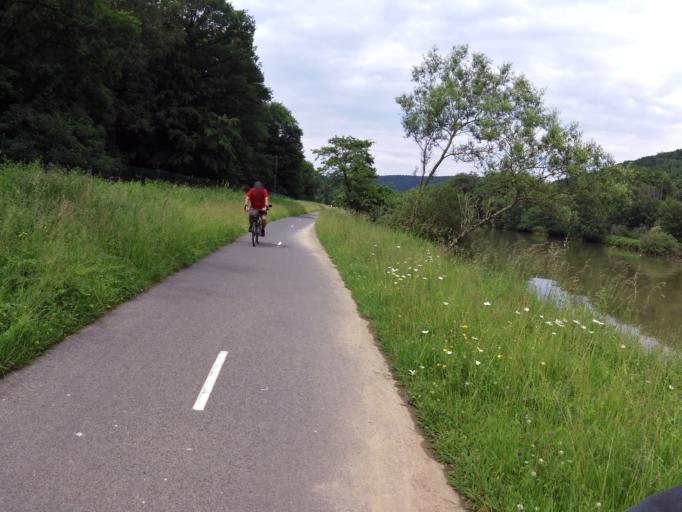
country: FR
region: Champagne-Ardenne
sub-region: Departement des Ardennes
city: Nouzonville
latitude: 49.8031
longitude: 4.7503
